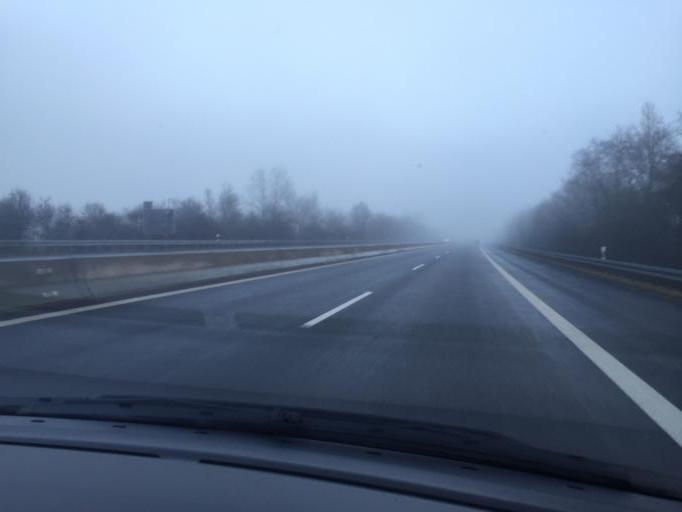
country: DE
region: Baden-Wuerttemberg
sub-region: Freiburg Region
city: Geisingen
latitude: 47.9532
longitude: 8.6193
